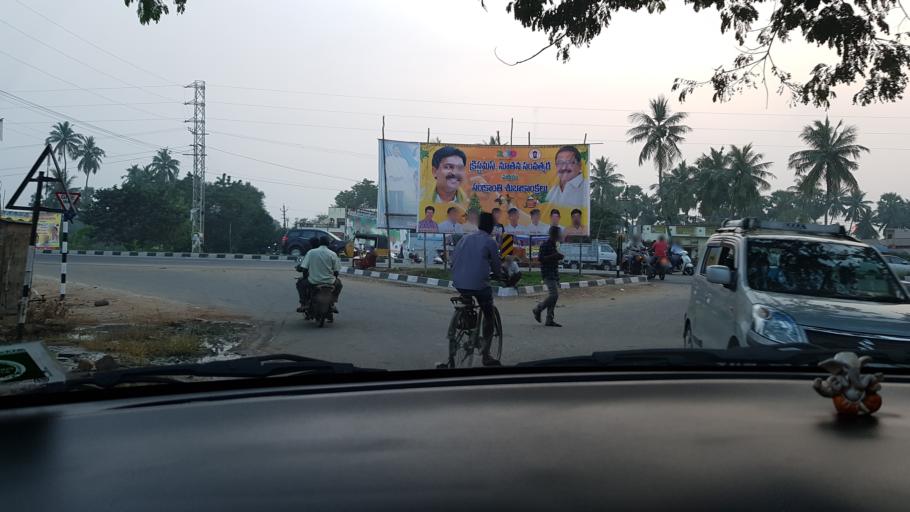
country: IN
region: Andhra Pradesh
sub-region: Krishna
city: Kankipadu
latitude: 16.4510
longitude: 80.7457
